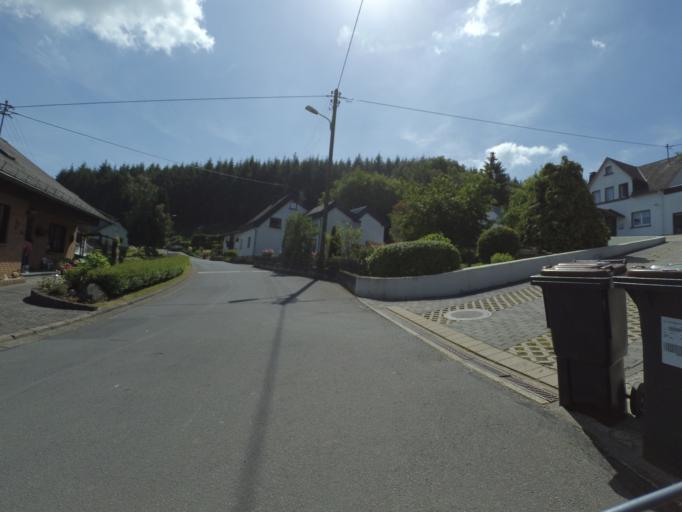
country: DE
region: Rheinland-Pfalz
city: Bermel
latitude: 50.2826
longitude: 7.0887
